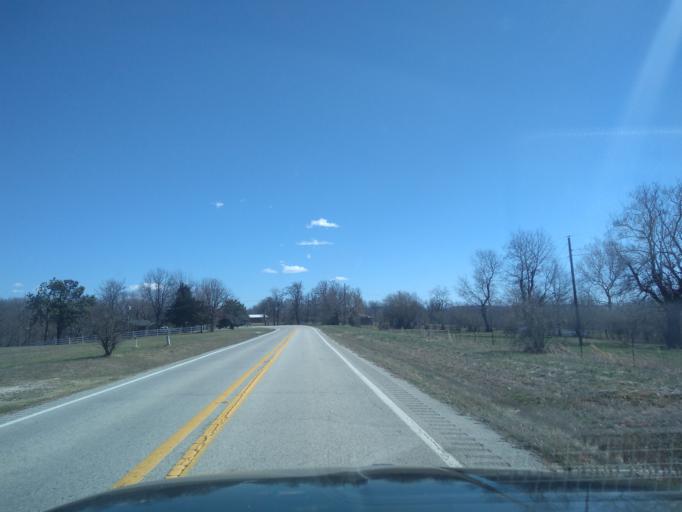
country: US
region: Arkansas
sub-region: Washington County
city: Farmington
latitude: 36.0806
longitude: -94.3094
